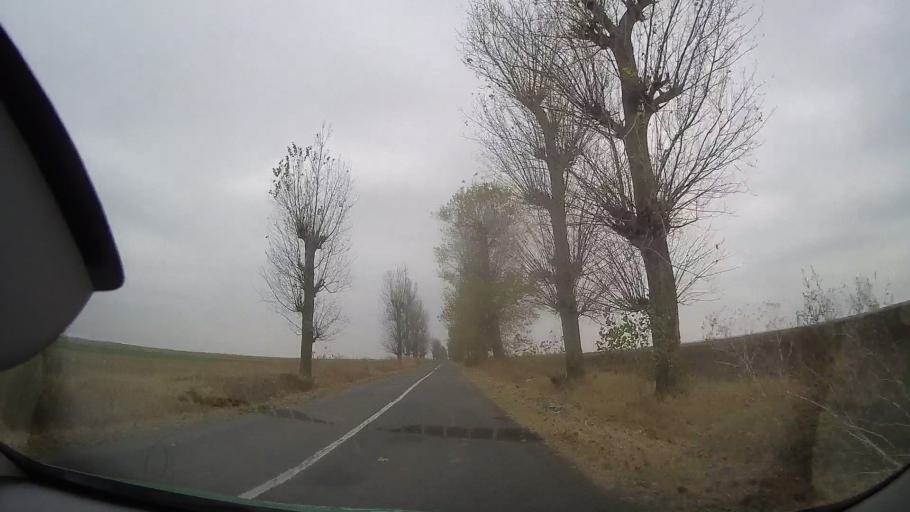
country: RO
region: Ialomita
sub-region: Comuna Grindu
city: Grindu
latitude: 44.7735
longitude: 26.8867
